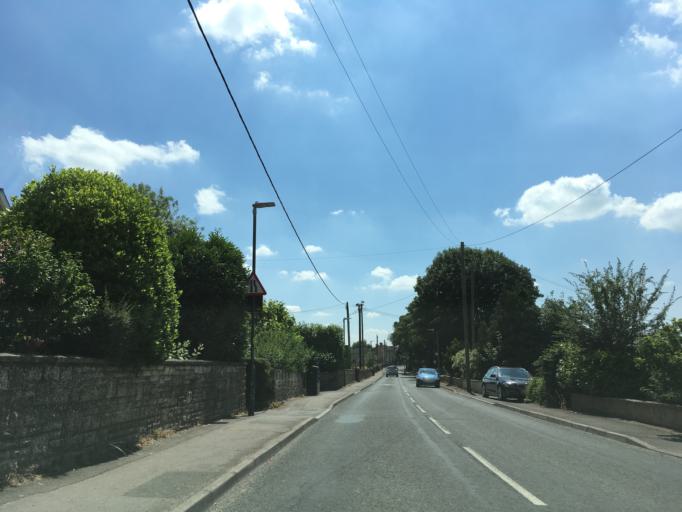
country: GB
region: England
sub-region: Gloucestershire
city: Stroud
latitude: 51.7588
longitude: -2.2320
